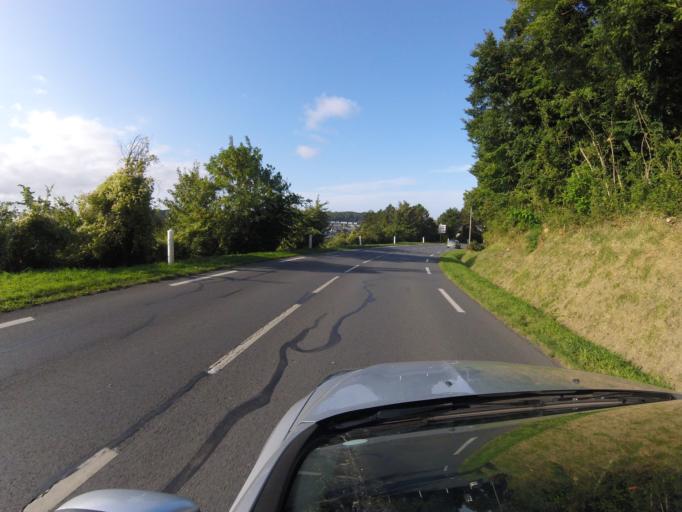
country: FR
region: Haute-Normandie
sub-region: Departement de la Seine-Maritime
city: Fecamp
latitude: 49.7595
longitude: 0.3927
